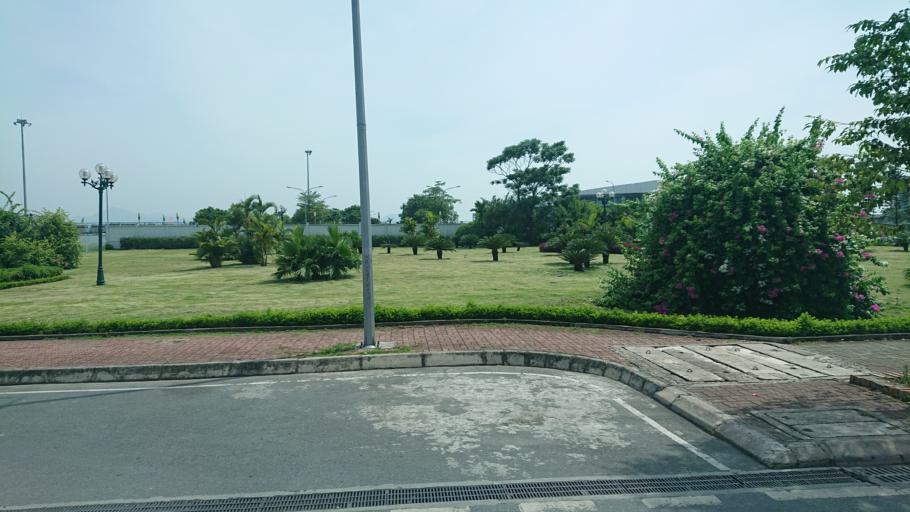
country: VN
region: Ha Noi
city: Soc Son
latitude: 21.2145
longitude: 105.7983
